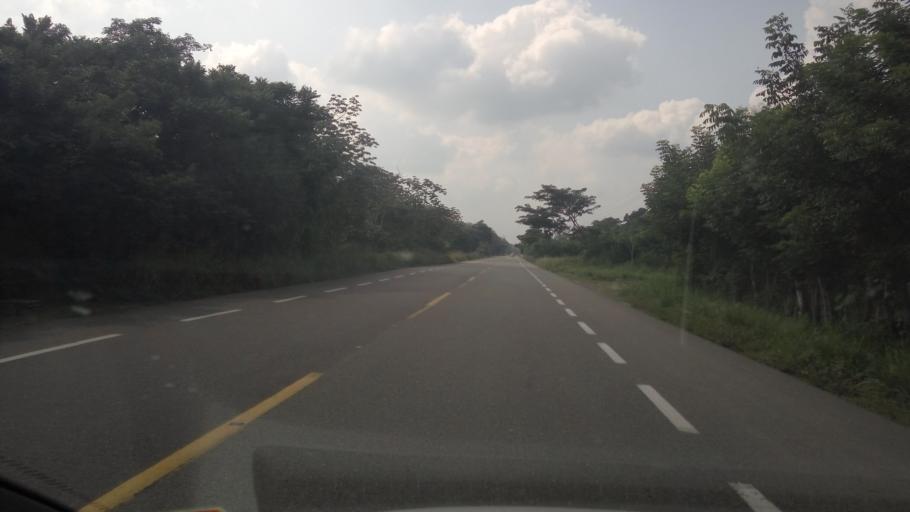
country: MX
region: Tabasco
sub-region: Centla
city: Alvaro Obregon 2da. Seccion (El Lechugal)
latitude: 18.4518
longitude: -92.7749
